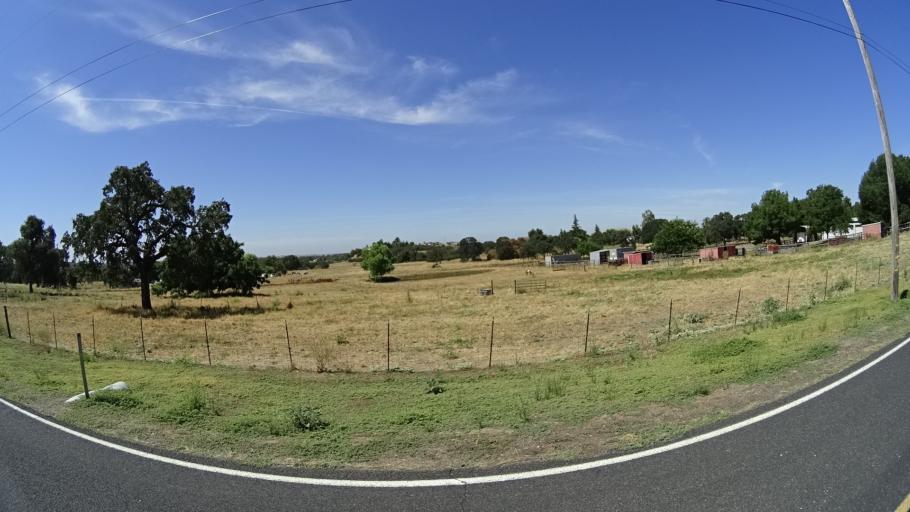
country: US
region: California
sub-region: Calaveras County
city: Rancho Calaveras
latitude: 38.1475
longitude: -120.9314
